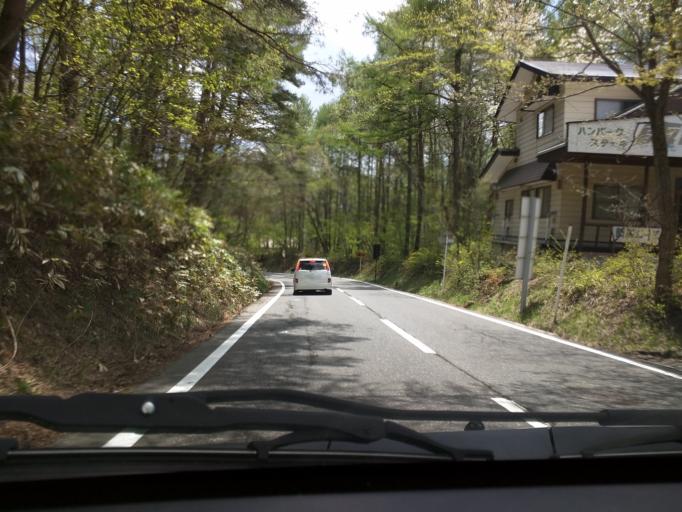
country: JP
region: Nagano
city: Nagano-shi
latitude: 36.7045
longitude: 138.1338
